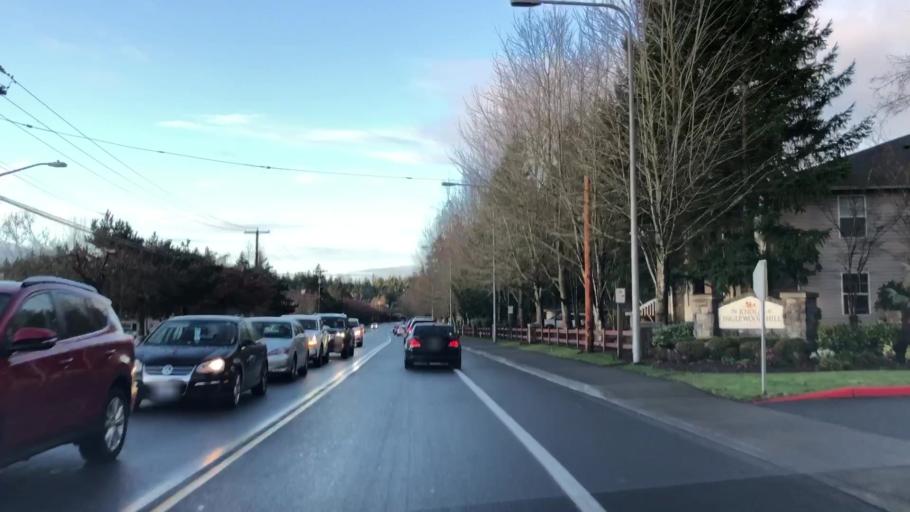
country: US
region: Washington
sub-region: King County
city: City of Sammamish
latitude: 47.6164
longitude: -122.0361
